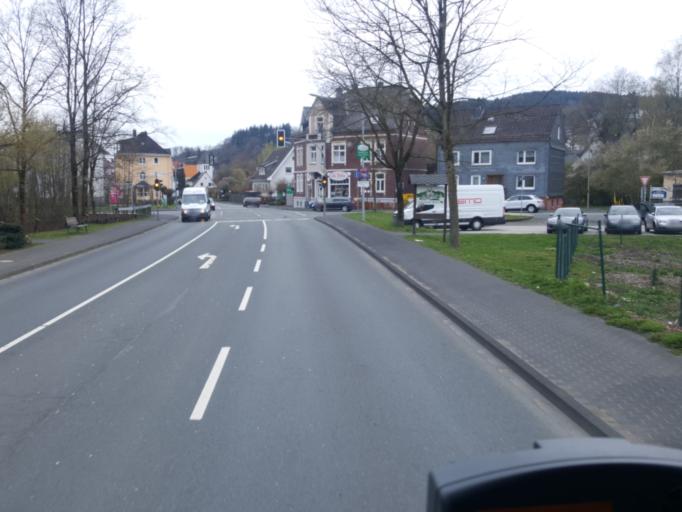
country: DE
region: North Rhine-Westphalia
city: Hilchenbach
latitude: 50.9958
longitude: 8.1107
